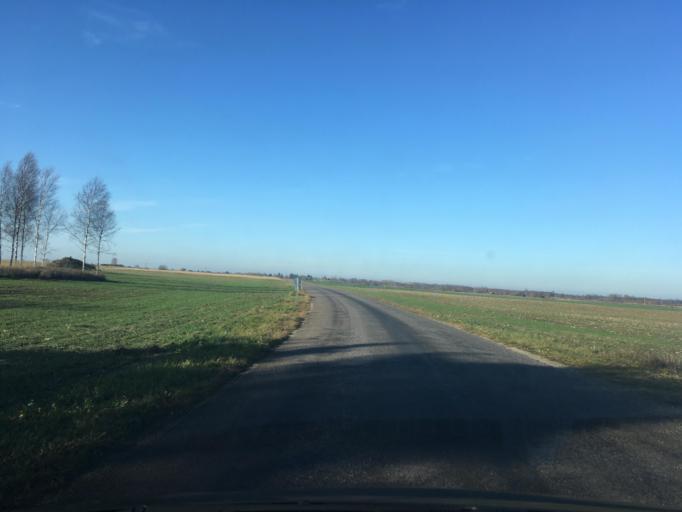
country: EE
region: Harju
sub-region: Raasiku vald
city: Arukula
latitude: 59.4501
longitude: 25.1165
